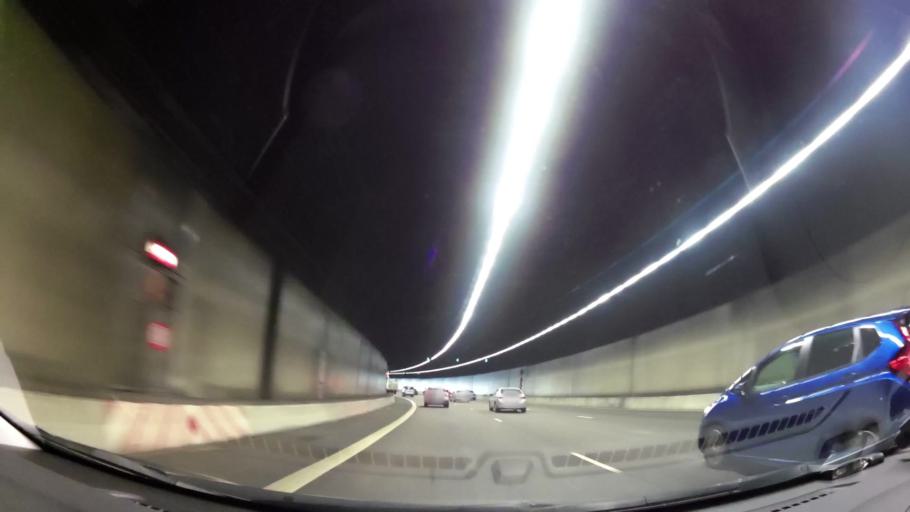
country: SG
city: Singapore
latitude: 1.3051
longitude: 103.8418
